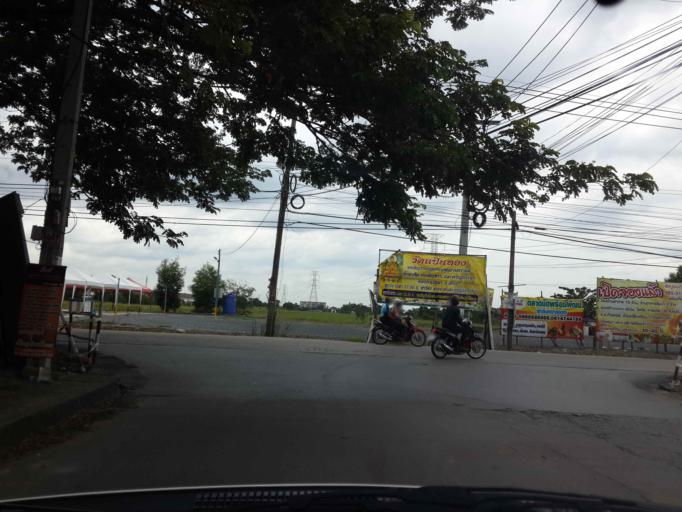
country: TH
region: Bangkok
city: Khlong Sam Wa
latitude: 13.8862
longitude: 100.7114
